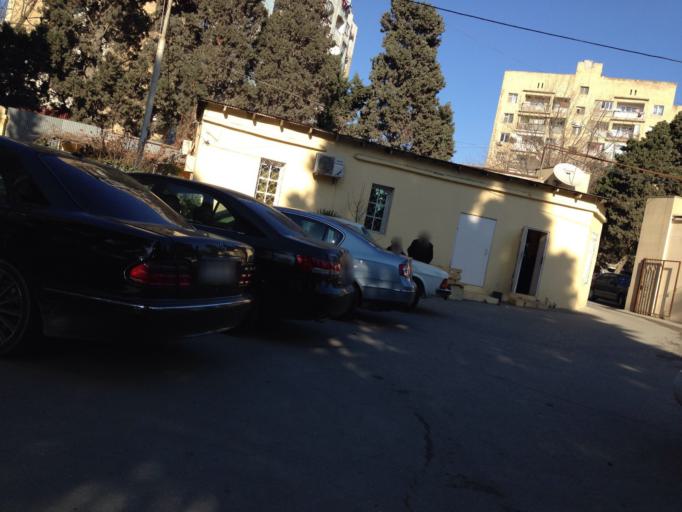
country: AZ
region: Baki
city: Baku
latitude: 40.3918
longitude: 49.8758
